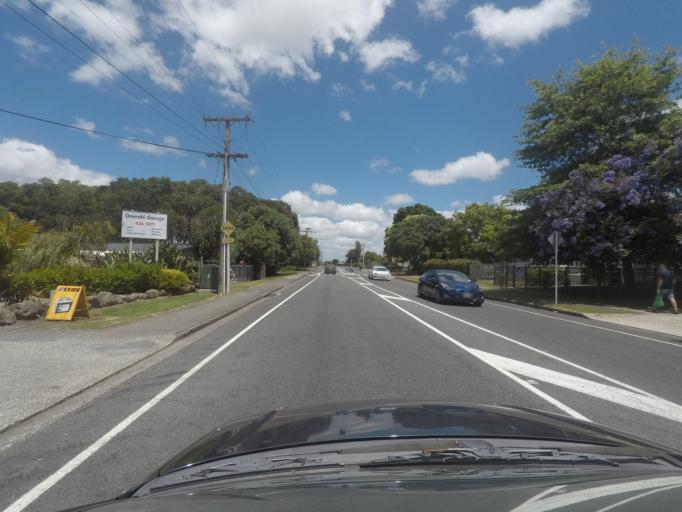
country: NZ
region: Northland
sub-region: Whangarei
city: Whangarei
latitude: -35.7576
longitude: 174.3679
